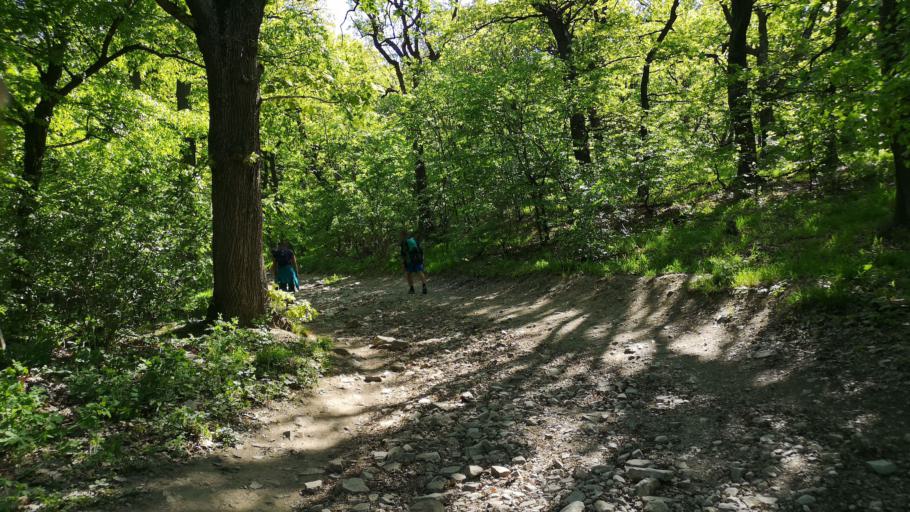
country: SK
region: Nitriansky
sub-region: Okres Nitra
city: Nitra
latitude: 48.3435
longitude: 18.0981
